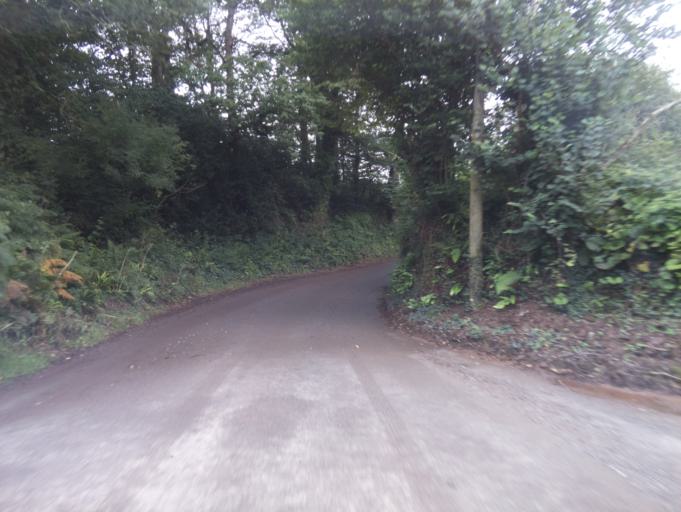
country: GB
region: England
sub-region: Devon
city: Kingsbridge
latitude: 50.2765
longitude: -3.7195
